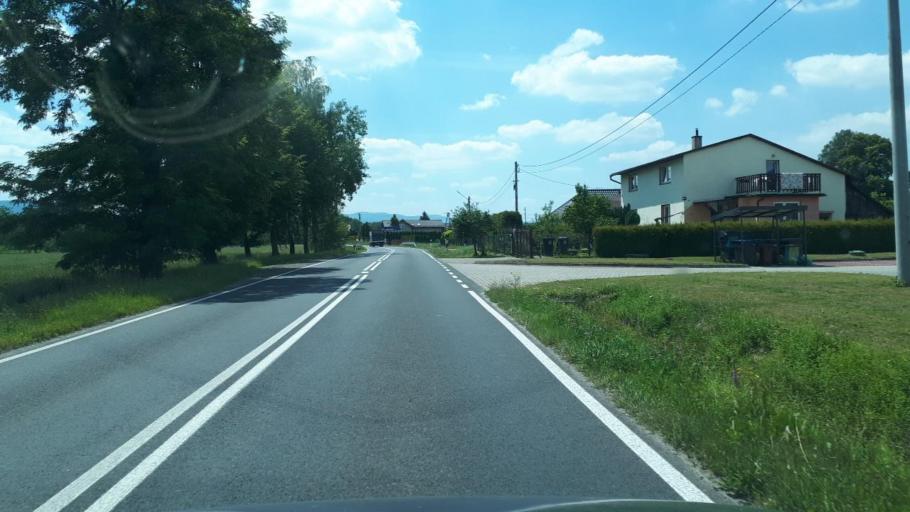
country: PL
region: Silesian Voivodeship
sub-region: Powiat bielski
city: Pisarzowice
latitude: 49.8997
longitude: 19.1456
